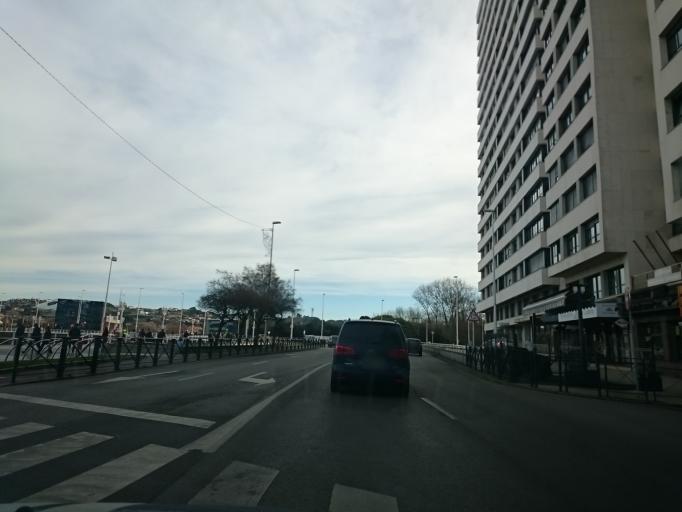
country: ES
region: Asturias
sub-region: Province of Asturias
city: Gijon
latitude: 43.5475
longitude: -5.6185
